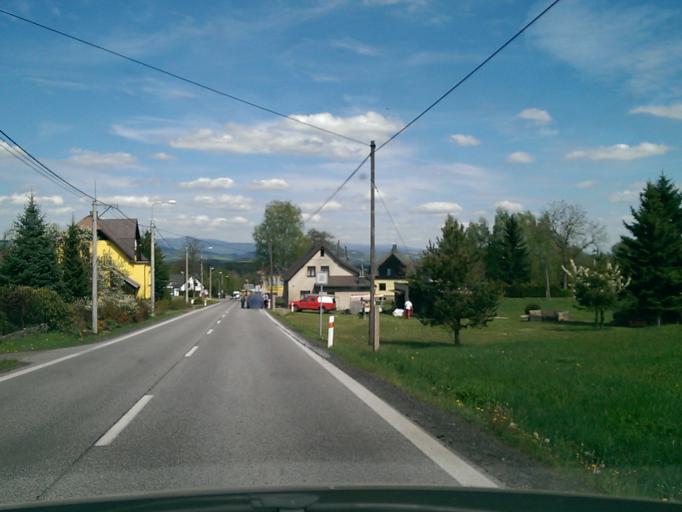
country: CZ
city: Pencin
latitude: 50.6862
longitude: 15.2294
